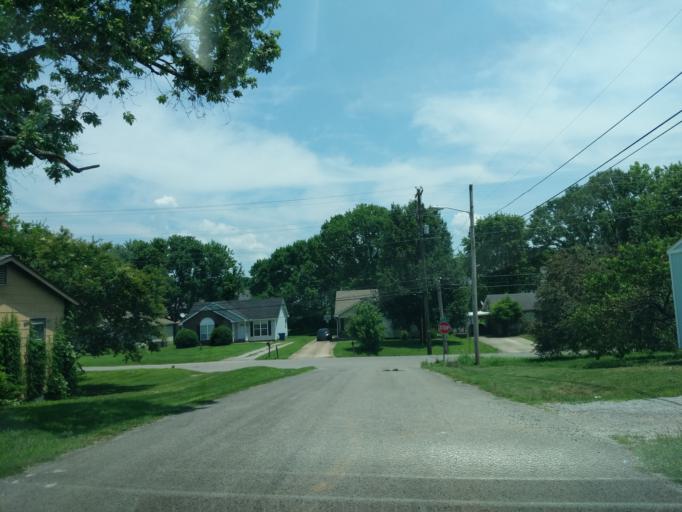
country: US
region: Tennessee
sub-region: Davidson County
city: Lakewood
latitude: 36.2404
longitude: -86.6384
